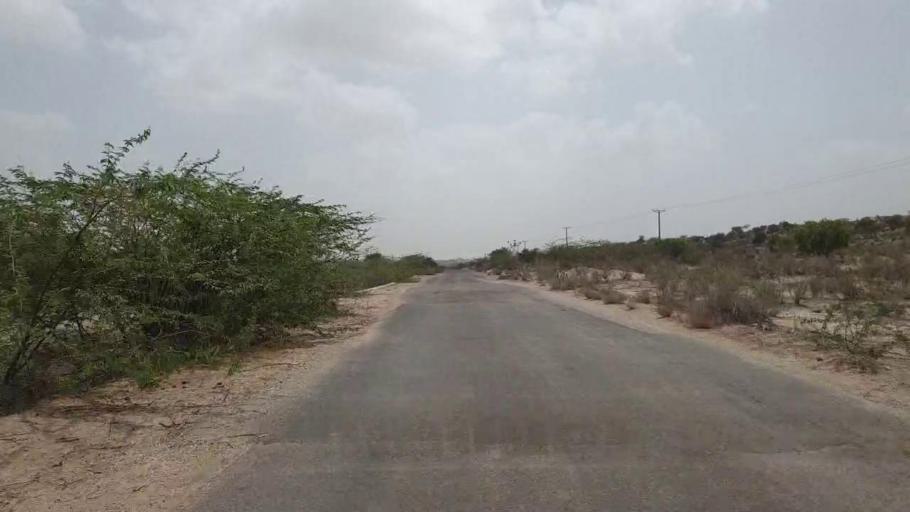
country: PK
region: Sindh
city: Diplo
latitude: 24.4028
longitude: 69.4739
